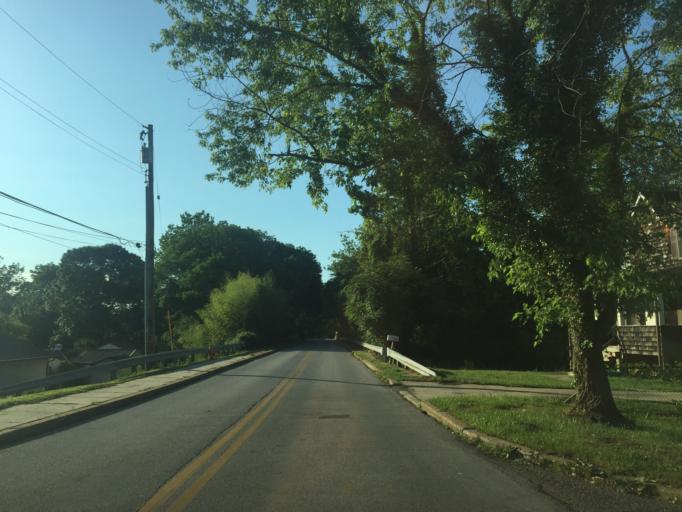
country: US
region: Maryland
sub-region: Howard County
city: Elkridge
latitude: 39.2248
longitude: -76.7064
